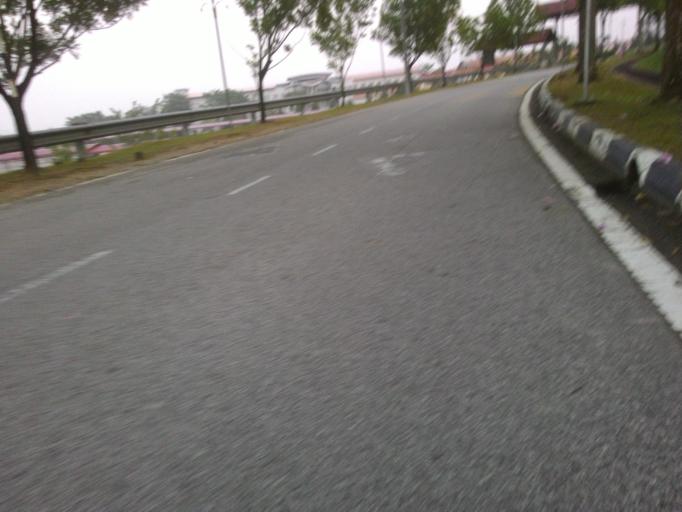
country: MY
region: Kedah
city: Kulim
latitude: 5.3830
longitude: 100.5761
